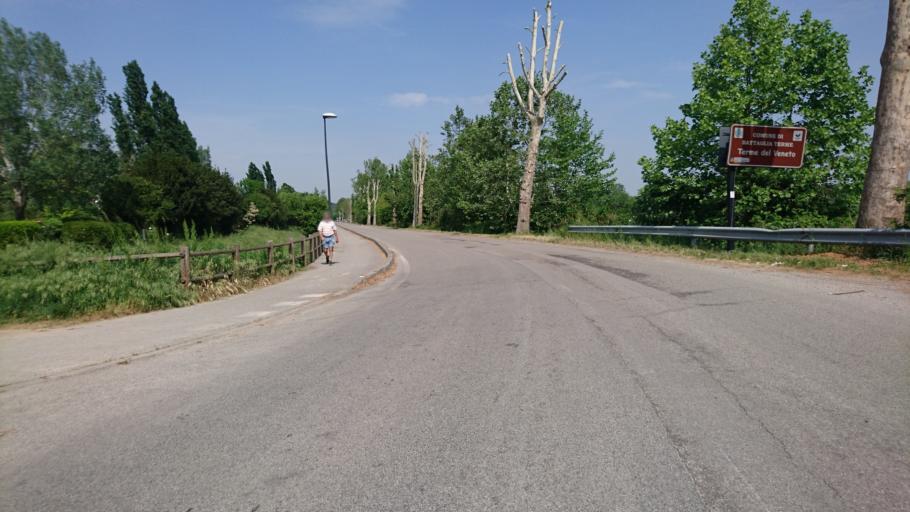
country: IT
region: Veneto
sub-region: Provincia di Padova
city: Battaglia Terme
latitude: 45.2865
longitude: 11.7661
